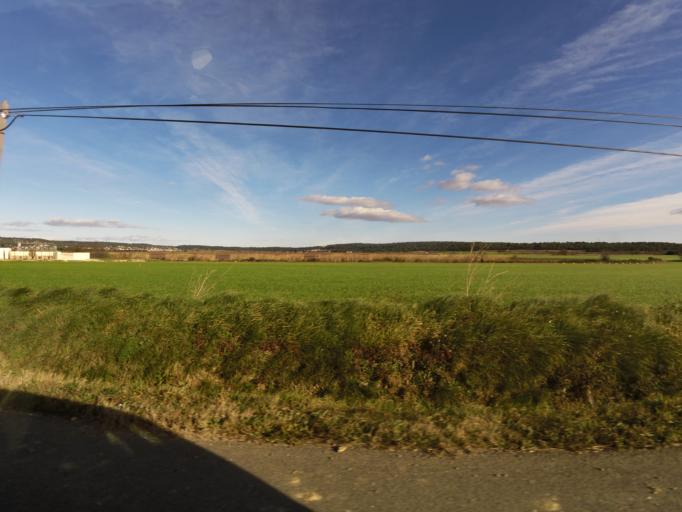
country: FR
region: Languedoc-Roussillon
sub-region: Departement du Gard
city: Calvisson
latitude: 43.7680
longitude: 4.2011
